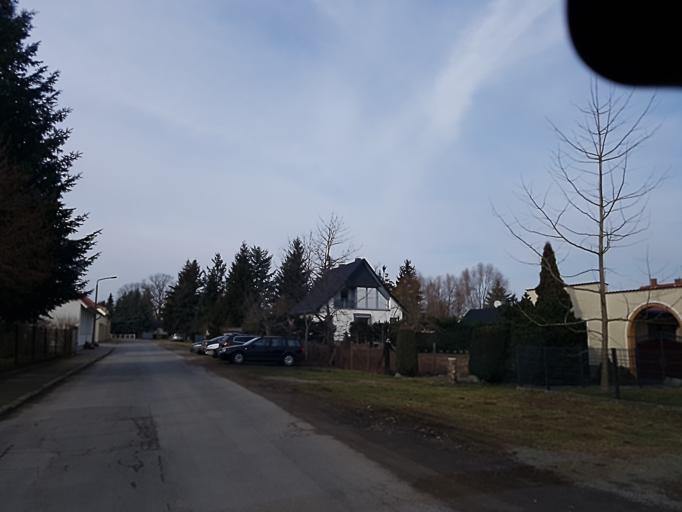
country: DE
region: Brandenburg
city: Doberlug-Kirchhain
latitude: 51.6129
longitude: 13.5531
